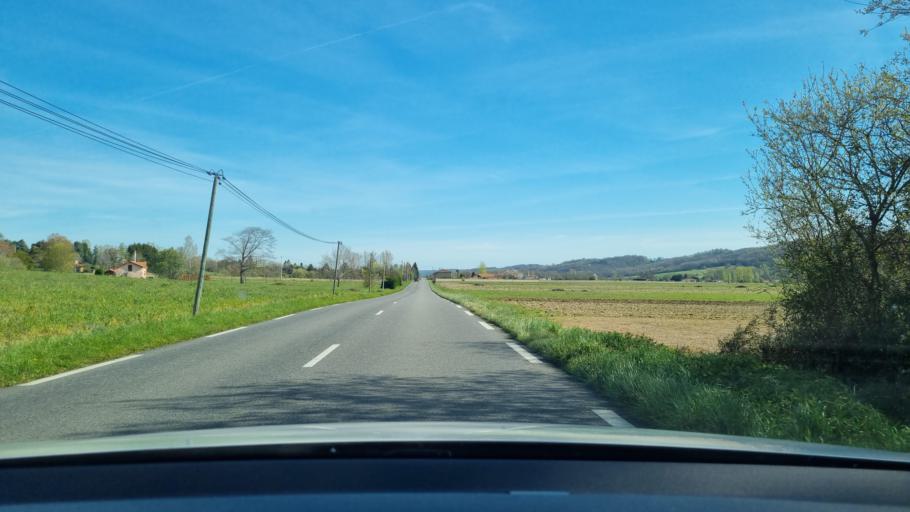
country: FR
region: Midi-Pyrenees
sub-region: Departement des Hautes-Pyrenees
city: Lannemezan
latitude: 43.2193
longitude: 0.4764
